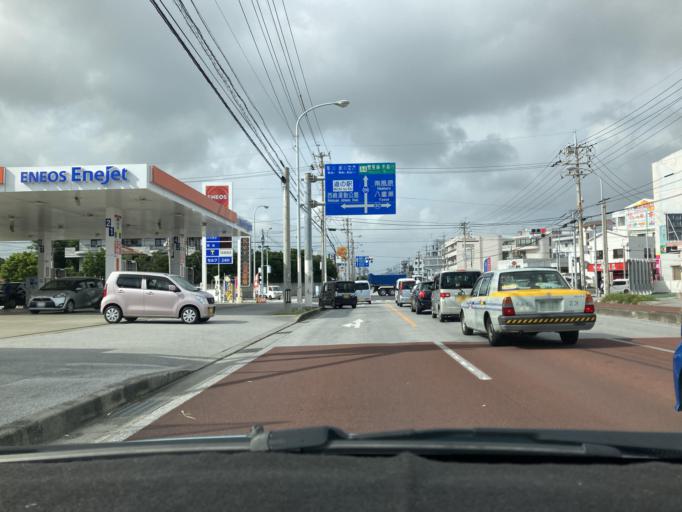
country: JP
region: Okinawa
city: Itoman
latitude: 26.1501
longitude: 127.6725
